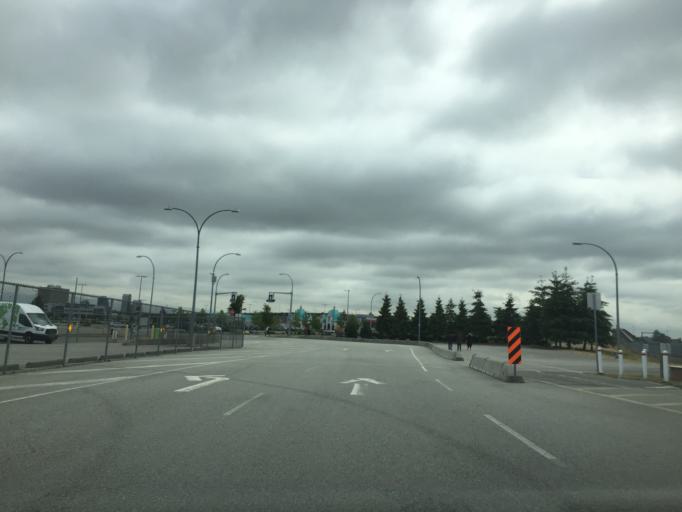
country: CA
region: British Columbia
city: Richmond
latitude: 49.1971
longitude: -123.1462
